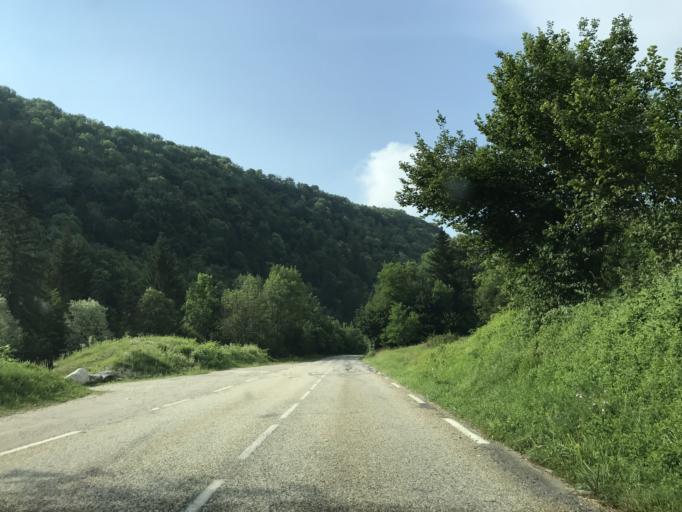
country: FR
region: Rhone-Alpes
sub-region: Departement de l'Isere
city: Allevard
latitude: 45.4248
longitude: 6.0929
